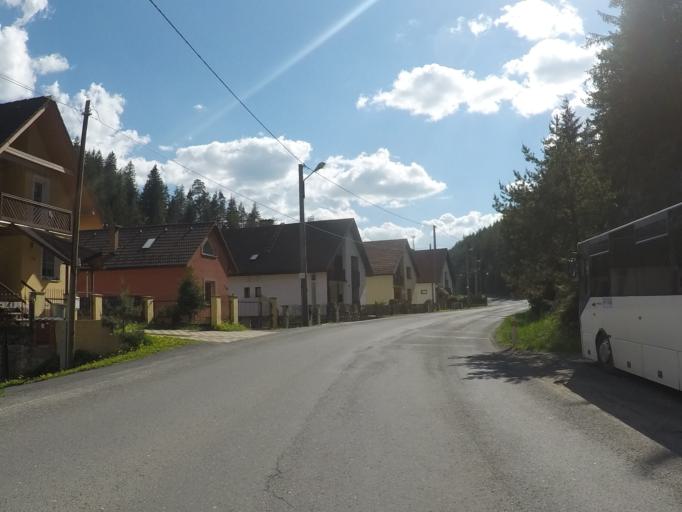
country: SK
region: Presovsky
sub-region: Okres Poprad
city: Poprad
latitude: 48.9257
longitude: 20.2776
